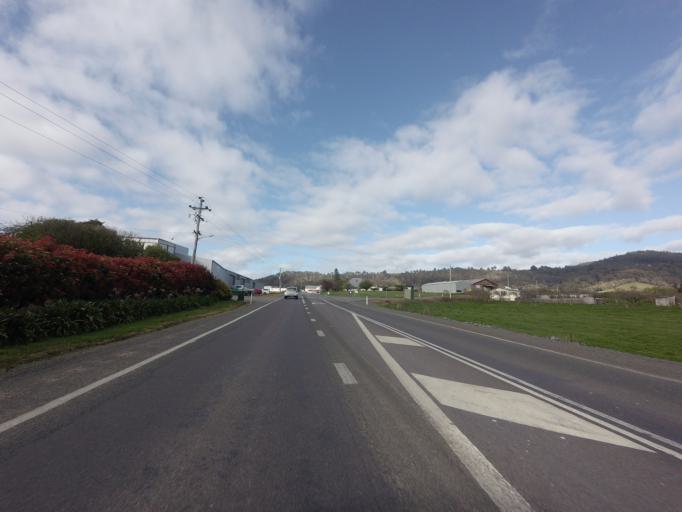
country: AU
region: Tasmania
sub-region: Huon Valley
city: Franklin
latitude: -43.1323
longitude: 146.9769
